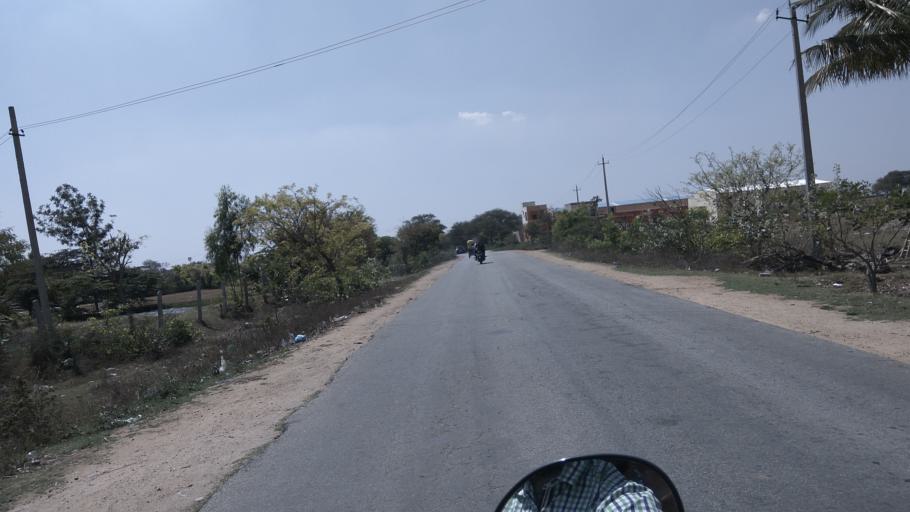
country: IN
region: Karnataka
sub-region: Kolar
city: Mulbagal
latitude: 13.1643
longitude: 78.3762
